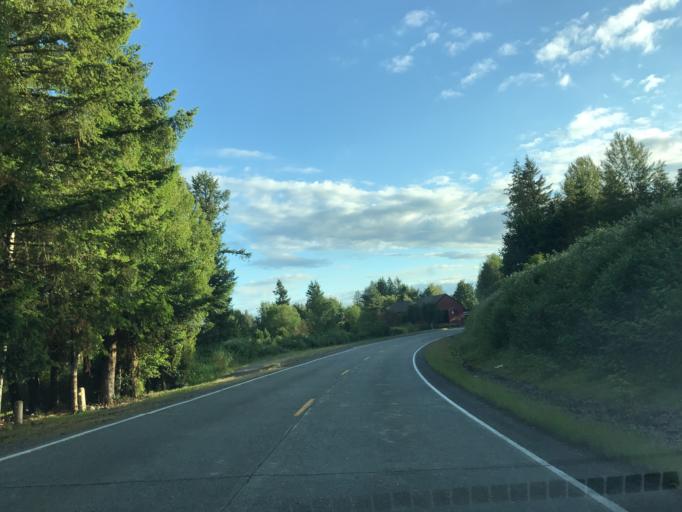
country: US
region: Washington
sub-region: King County
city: Black Diamond
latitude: 47.3133
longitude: -122.0107
